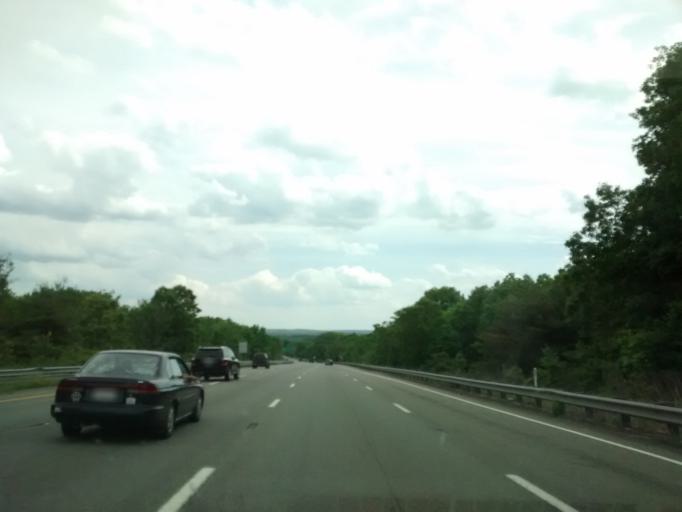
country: US
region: Massachusetts
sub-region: Worcester County
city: Cordaville
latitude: 42.2842
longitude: -71.5671
